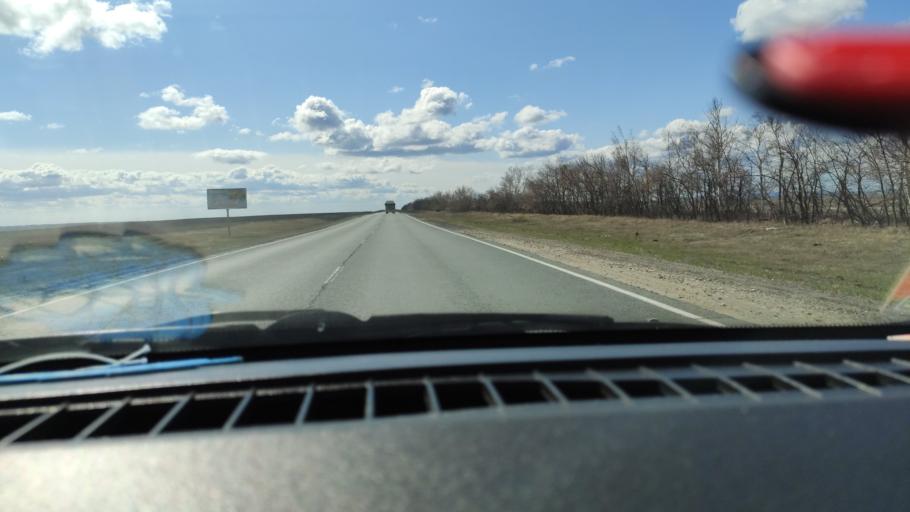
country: RU
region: Saratov
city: Dukhovnitskoye
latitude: 52.7937
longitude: 48.2316
